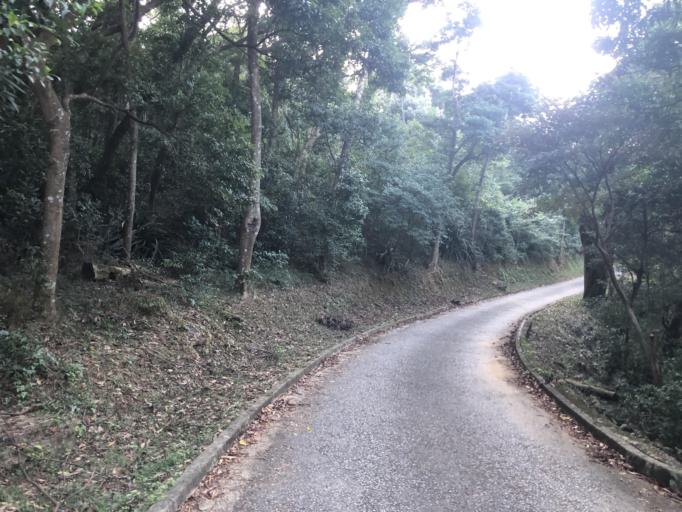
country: HK
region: Tsuen Wan
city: Tsuen Wan
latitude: 22.3965
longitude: 114.0772
